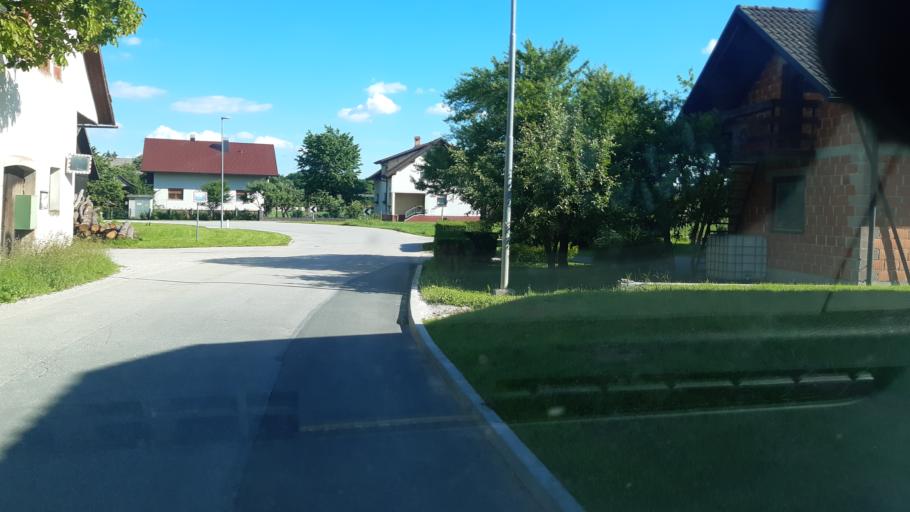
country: SI
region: Sencur
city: Hrastje
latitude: 46.2105
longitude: 14.3880
